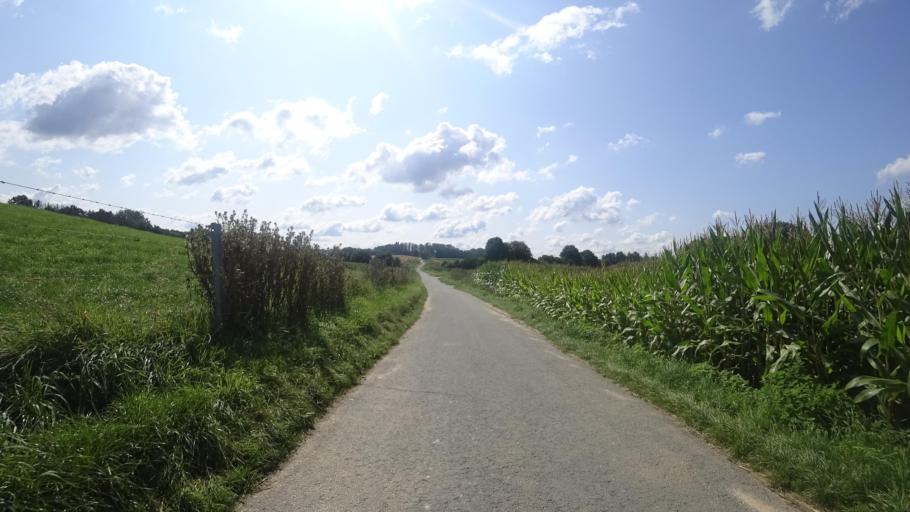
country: BE
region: Flanders
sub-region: Provincie Vlaams-Brabant
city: Tervuren
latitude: 50.8282
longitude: 4.5557
